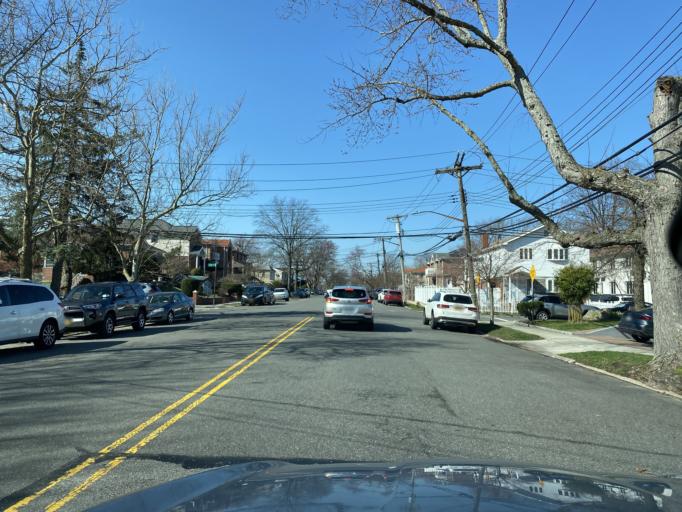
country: US
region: New York
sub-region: Nassau County
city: Lake Success
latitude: 40.7502
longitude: -73.7456
